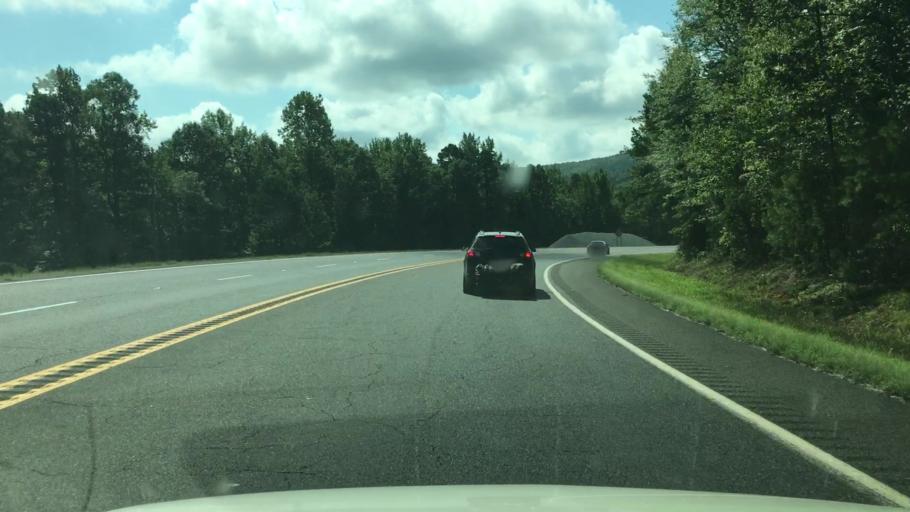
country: US
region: Arkansas
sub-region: Garland County
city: Lake Hamilton
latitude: 34.3680
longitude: -93.1627
